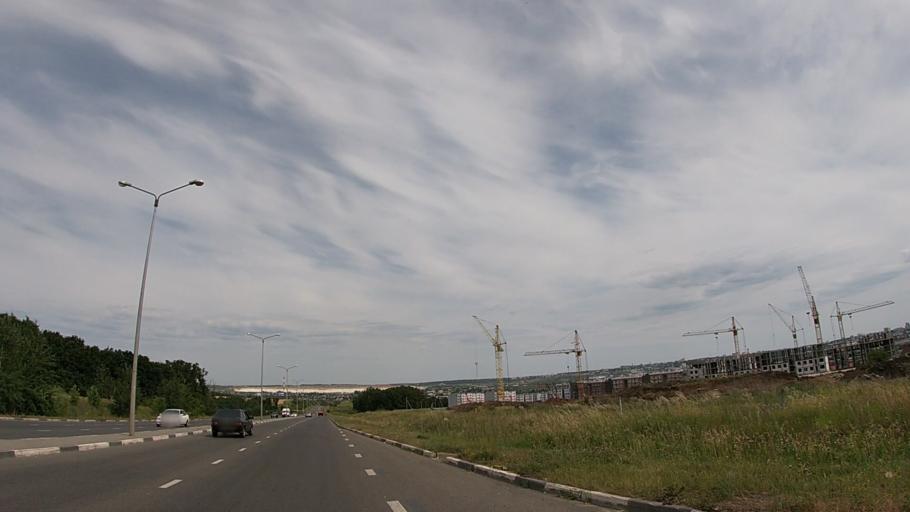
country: RU
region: Belgorod
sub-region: Belgorodskiy Rayon
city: Belgorod
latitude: 50.5949
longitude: 36.5309
